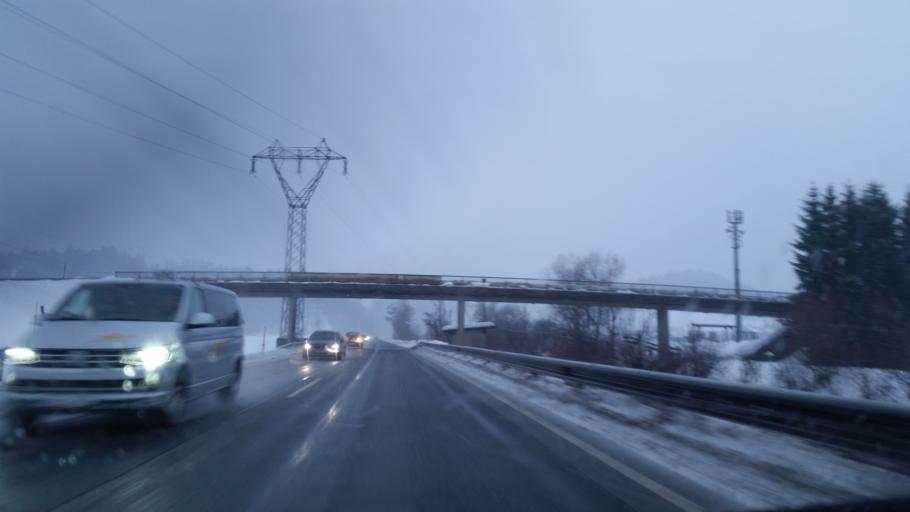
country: AT
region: Tyrol
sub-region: Politischer Bezirk Kitzbuhel
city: Sankt Johann in Tirol
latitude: 47.5190
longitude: 12.4034
